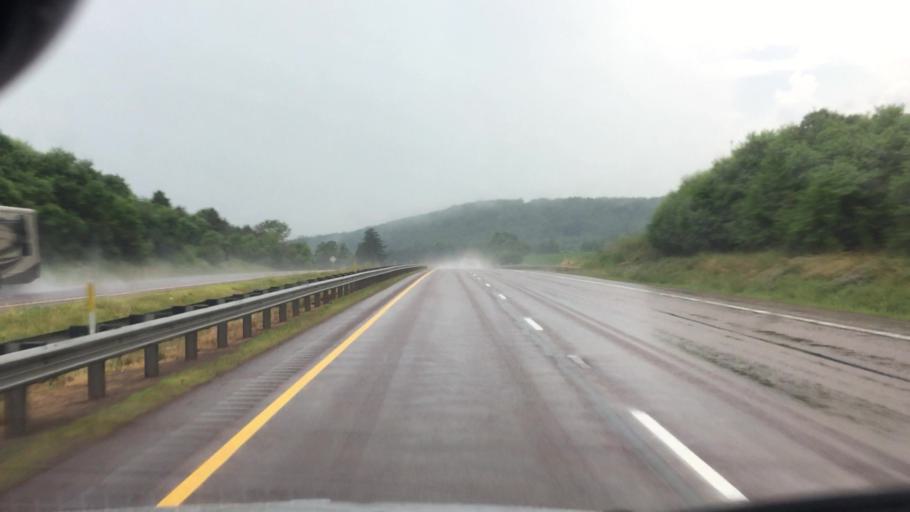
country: US
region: Pennsylvania
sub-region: Somerset County
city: Meyersdale
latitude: 39.7010
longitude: -79.2986
